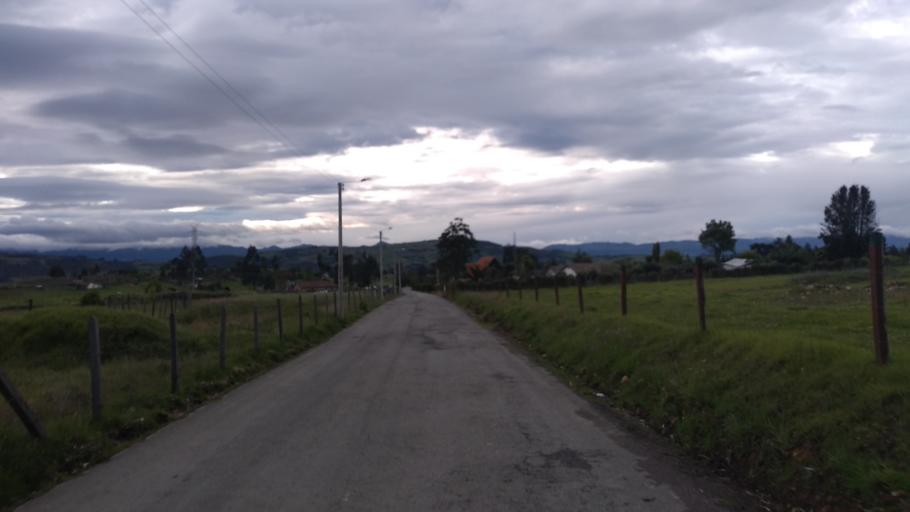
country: CO
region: Boyaca
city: Toca
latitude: 5.5791
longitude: -73.1836
